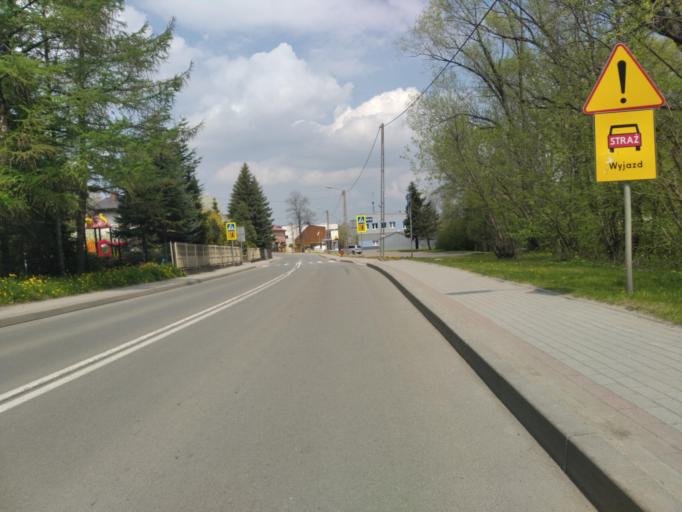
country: PL
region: Subcarpathian Voivodeship
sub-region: Powiat krosnienski
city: Rymanow
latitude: 49.5717
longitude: 21.8673
